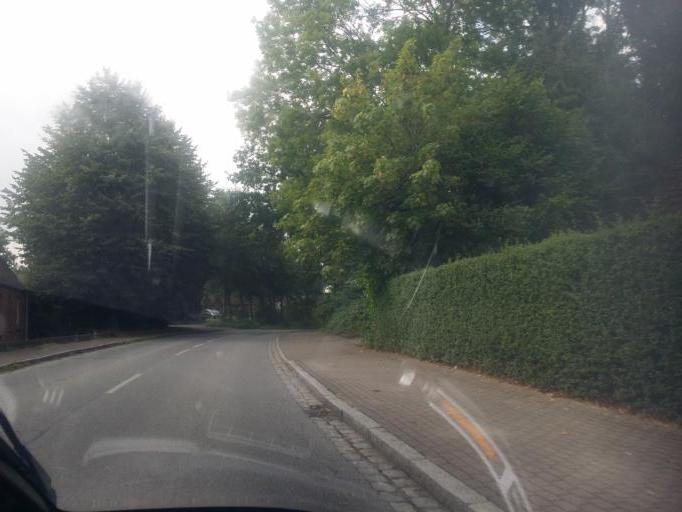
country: DE
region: Schleswig-Holstein
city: Kleve
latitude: 54.2953
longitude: 9.1208
